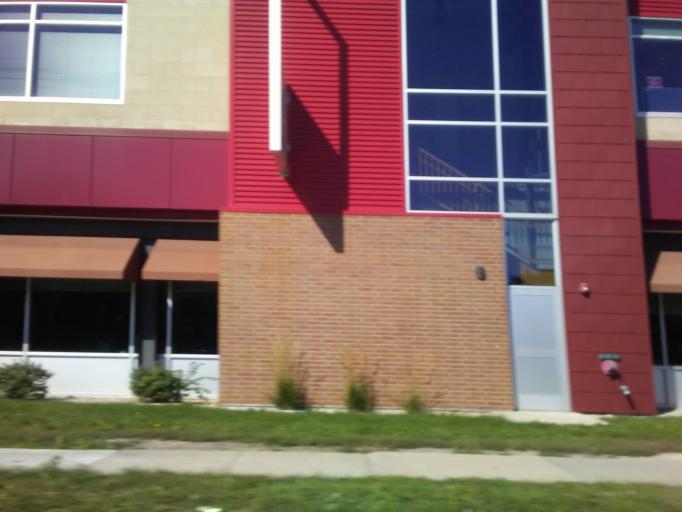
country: US
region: Wisconsin
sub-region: Dane County
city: Madison
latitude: 43.0415
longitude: -89.3942
